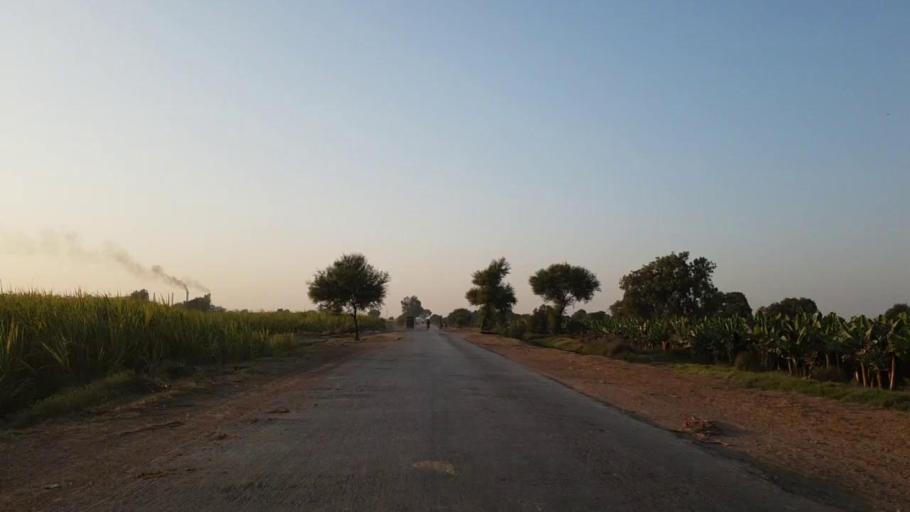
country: PK
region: Sindh
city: Chambar
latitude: 25.2467
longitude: 68.6824
